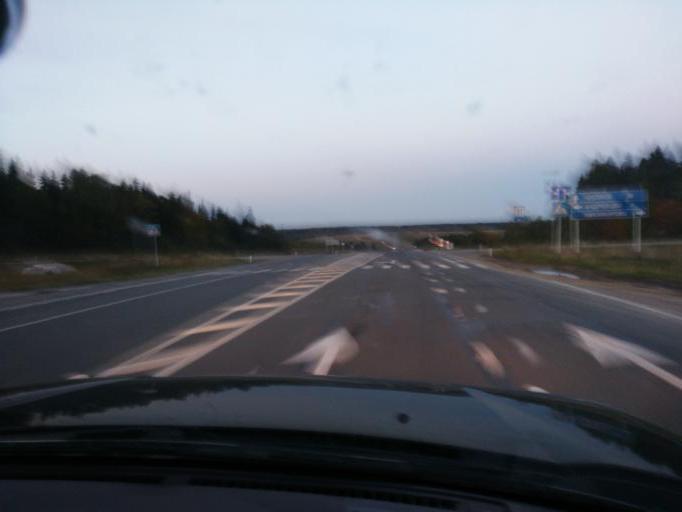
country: RU
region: Perm
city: Verkhnechusovskiye Gorodki
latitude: 58.2201
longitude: 57.1692
